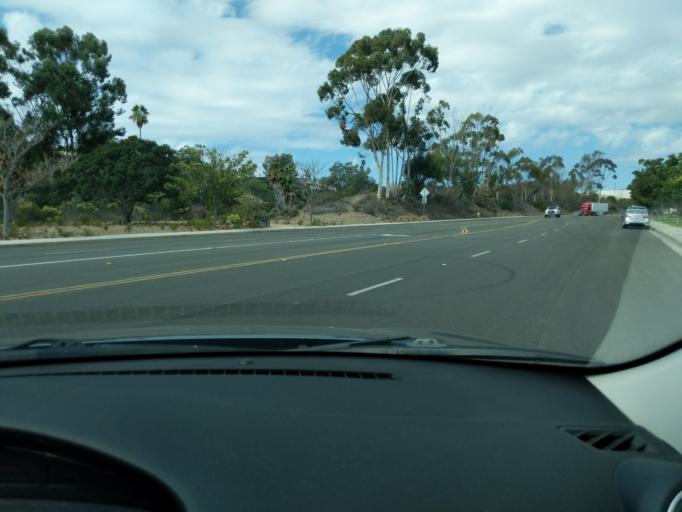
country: US
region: California
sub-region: San Diego County
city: San Diego
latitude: 32.8046
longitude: -117.1217
